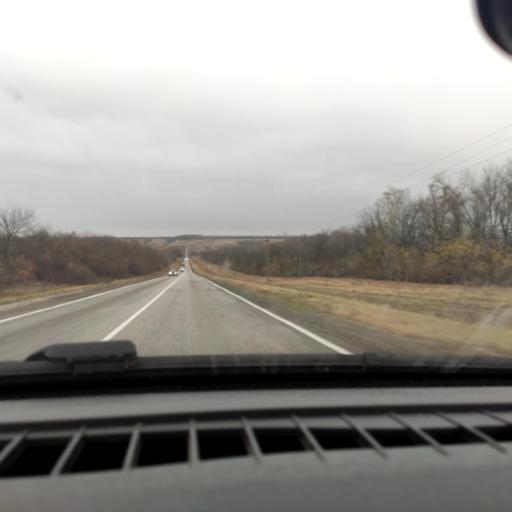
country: RU
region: Voronezj
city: Uryv-Pokrovka
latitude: 51.1164
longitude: 39.0306
